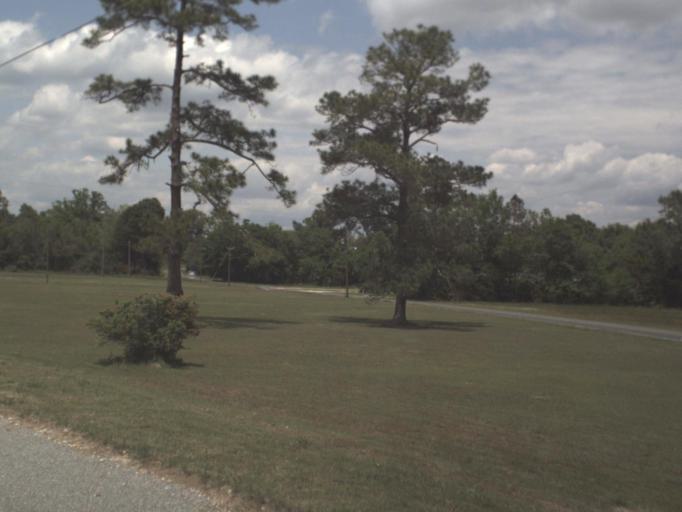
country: US
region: Alabama
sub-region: Escambia County
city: Atmore
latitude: 30.9993
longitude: -87.4887
